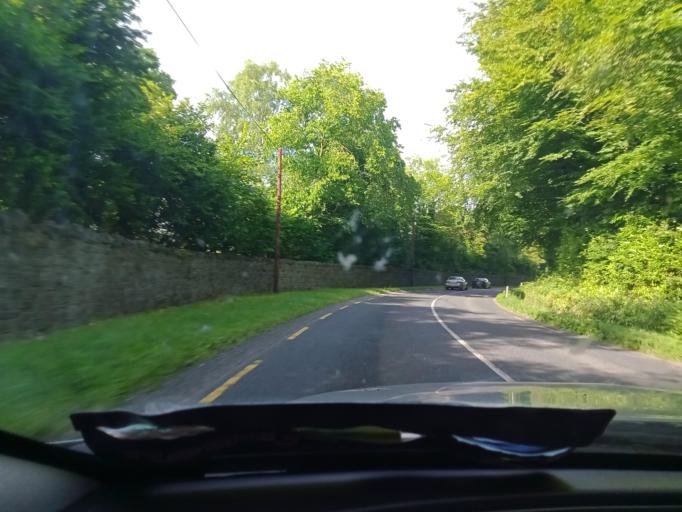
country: IE
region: Leinster
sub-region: An Iarmhi
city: An Muileann gCearr
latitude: 53.5737
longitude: -7.3240
